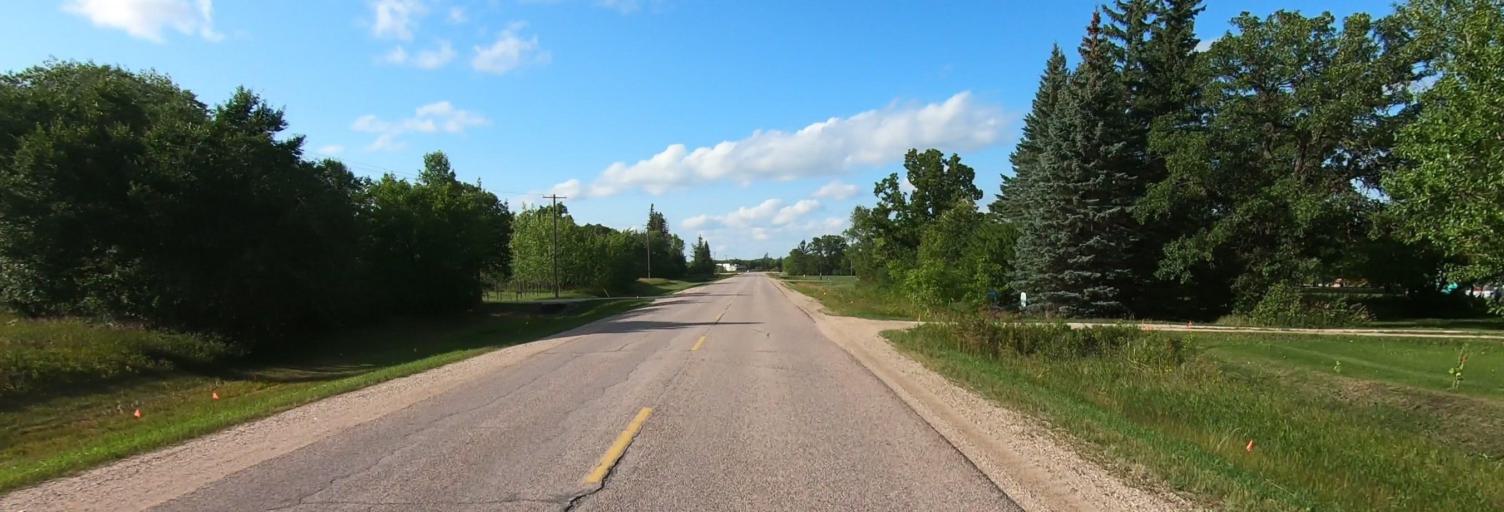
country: CA
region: Manitoba
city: Selkirk
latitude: 50.2075
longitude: -96.8402
